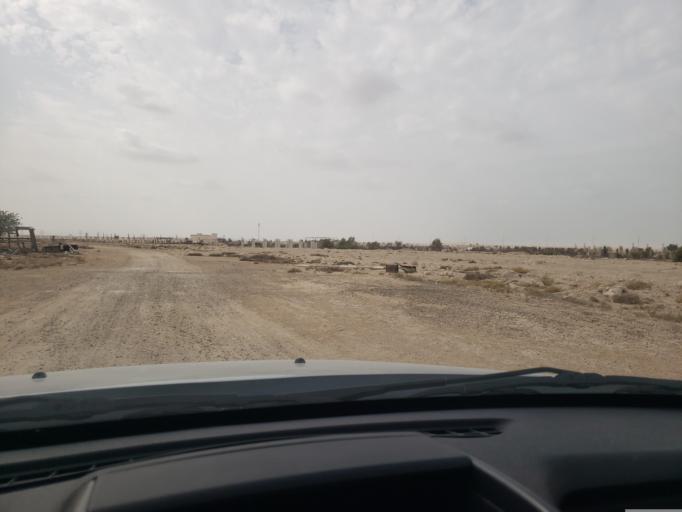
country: AE
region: Dubai
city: Dubai
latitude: 25.0008
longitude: 55.2476
